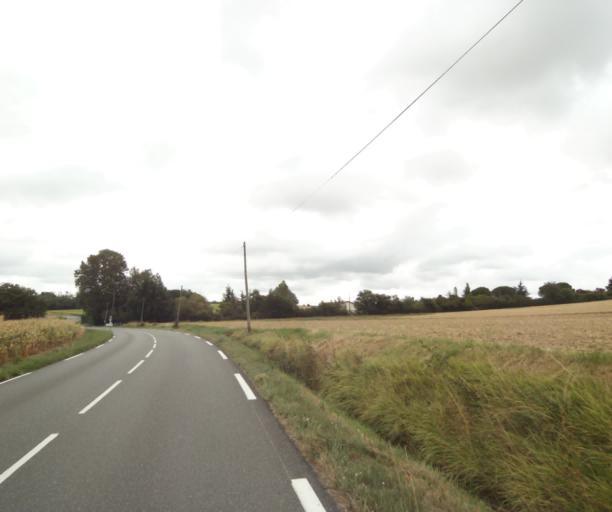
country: FR
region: Midi-Pyrenees
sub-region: Departement de la Haute-Garonne
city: Balma
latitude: 43.5989
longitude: 1.5169
